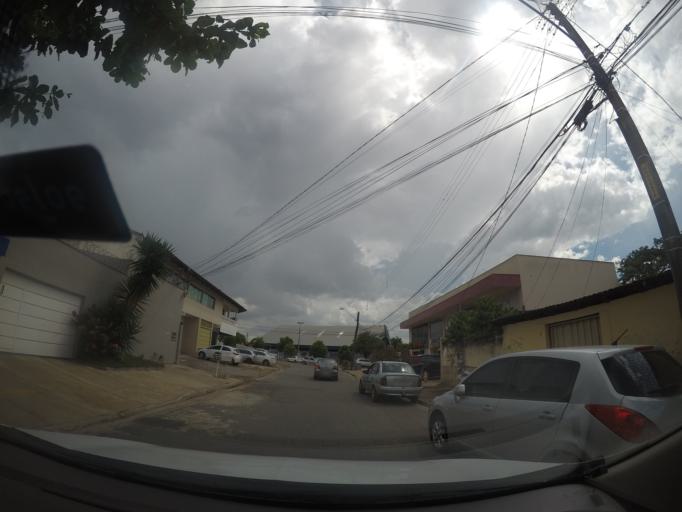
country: BR
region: Goias
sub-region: Goiania
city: Goiania
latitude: -16.7076
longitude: -49.2786
